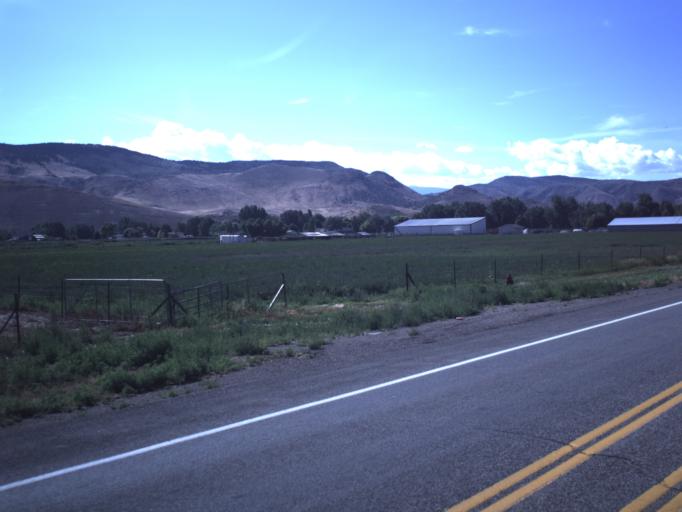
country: US
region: Utah
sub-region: Sevier County
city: Salina
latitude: 38.9672
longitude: -111.8601
